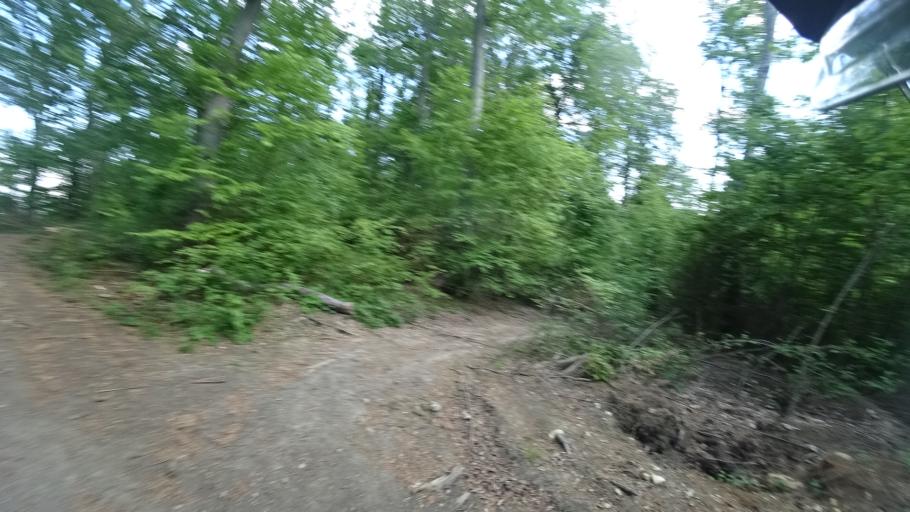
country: HR
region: Zagrebacka
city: Jablanovec
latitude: 45.8534
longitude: 15.8910
